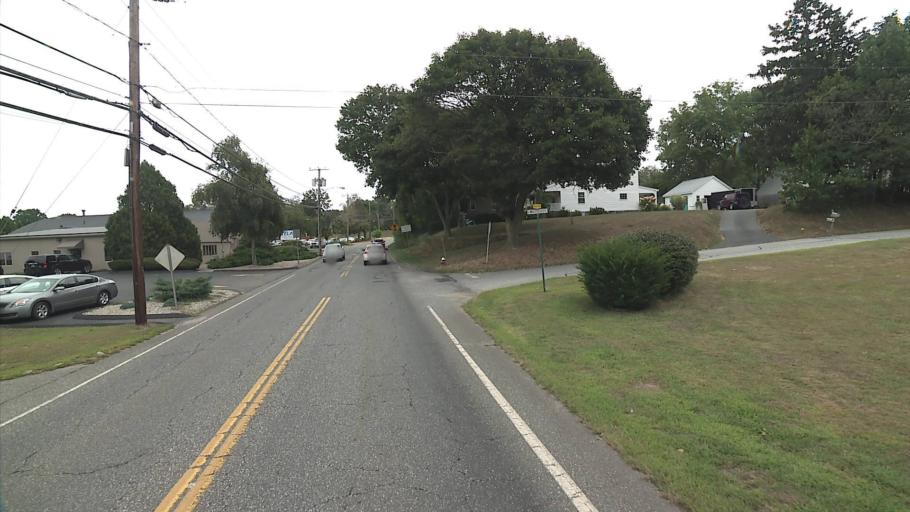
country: US
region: Connecticut
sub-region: New London County
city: Niantic
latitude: 41.3221
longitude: -72.2052
